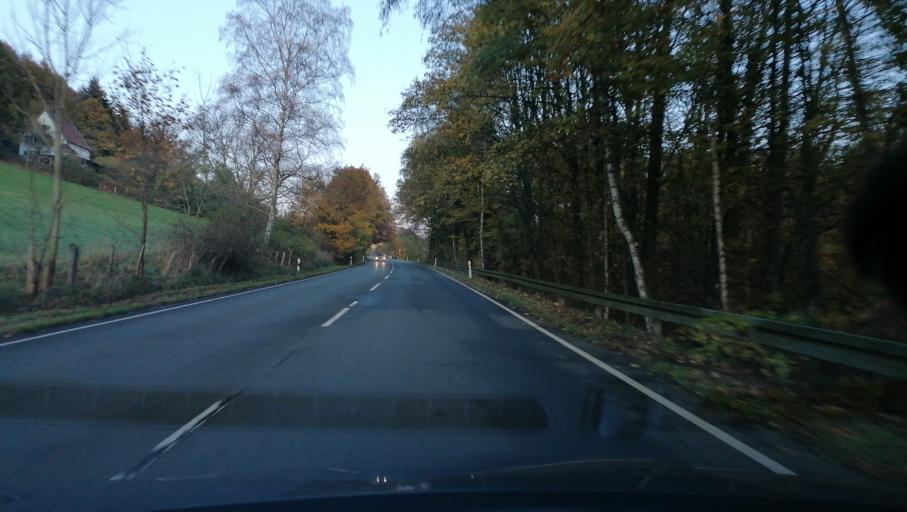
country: DE
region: North Rhine-Westphalia
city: Wetter (Ruhr)
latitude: 51.4073
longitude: 7.3891
